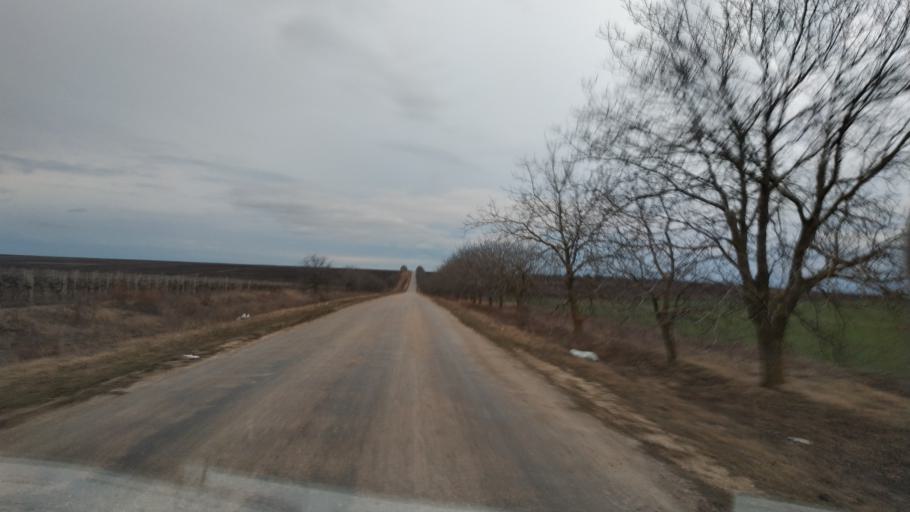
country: MD
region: Causeni
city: Causeni
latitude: 46.6072
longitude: 29.4011
